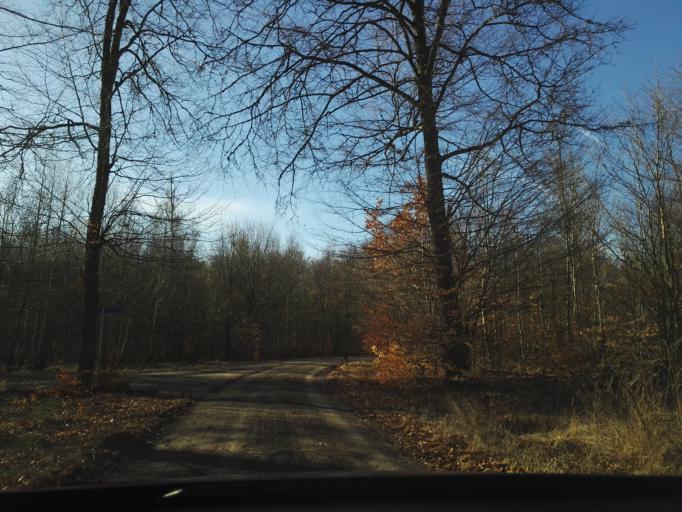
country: SE
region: Kronoberg
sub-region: Vaxjo Kommun
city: Vaexjoe
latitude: 56.9547
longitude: 14.7610
